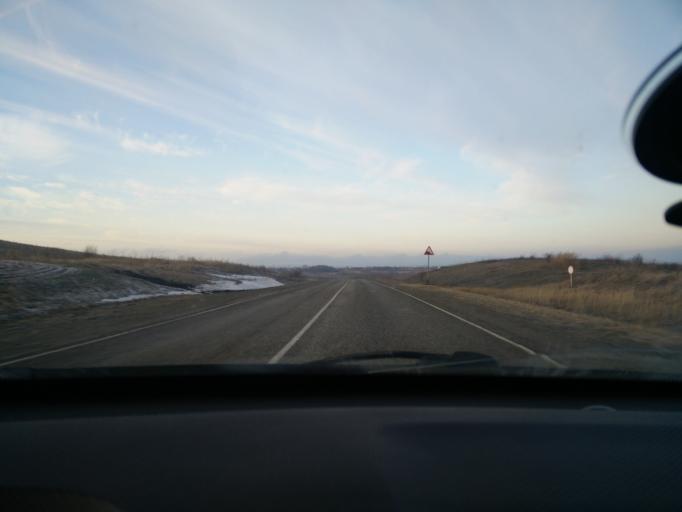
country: RU
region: Stavropol'skiy
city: Balakhonovskoye
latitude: 44.9905
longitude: 41.7091
